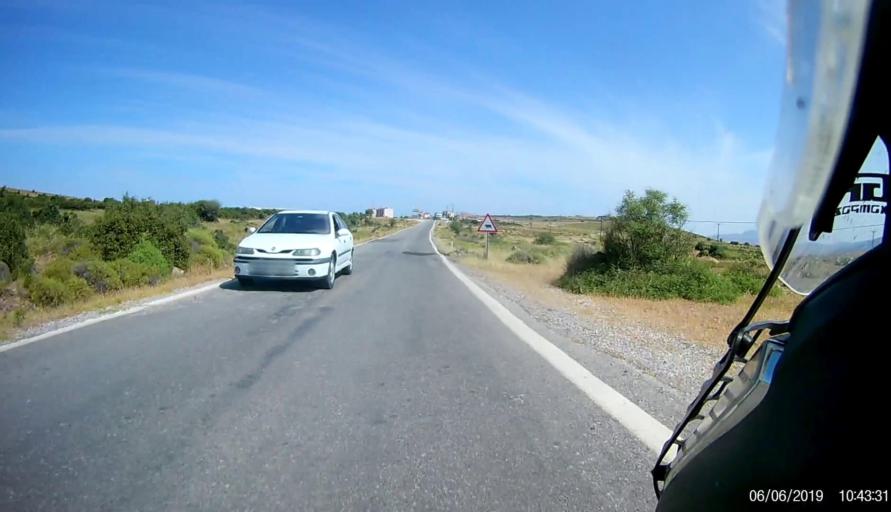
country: TR
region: Canakkale
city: Behram
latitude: 39.5073
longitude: 26.4214
